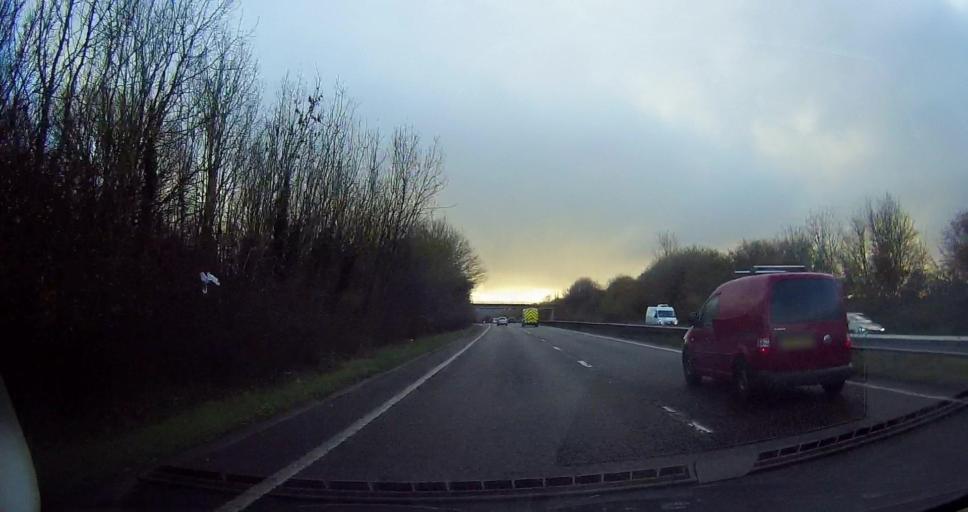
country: GB
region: England
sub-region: West Sussex
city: Hurstpierpoint
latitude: 50.9375
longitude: -0.1953
